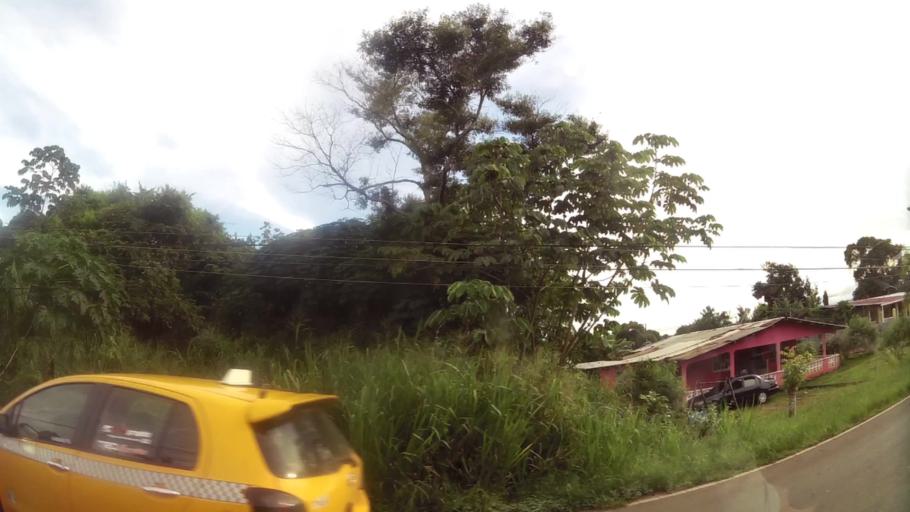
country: PA
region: Panama
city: La Chorrera
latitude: 8.8768
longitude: -79.7682
